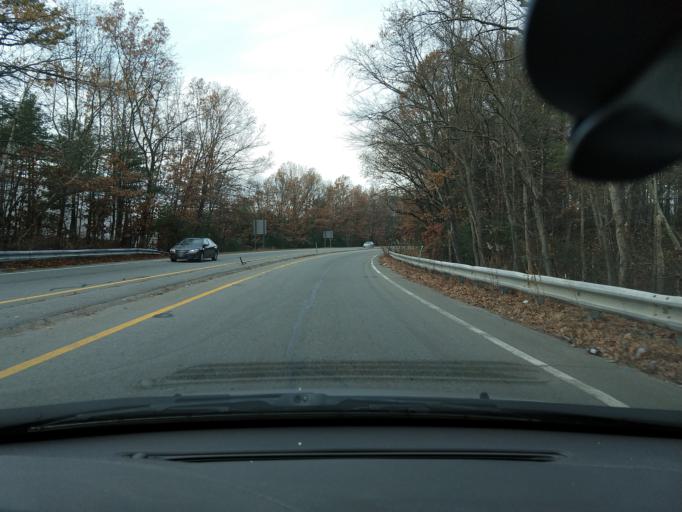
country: US
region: Massachusetts
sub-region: Middlesex County
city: Billerica
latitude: 42.5591
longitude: -71.2986
